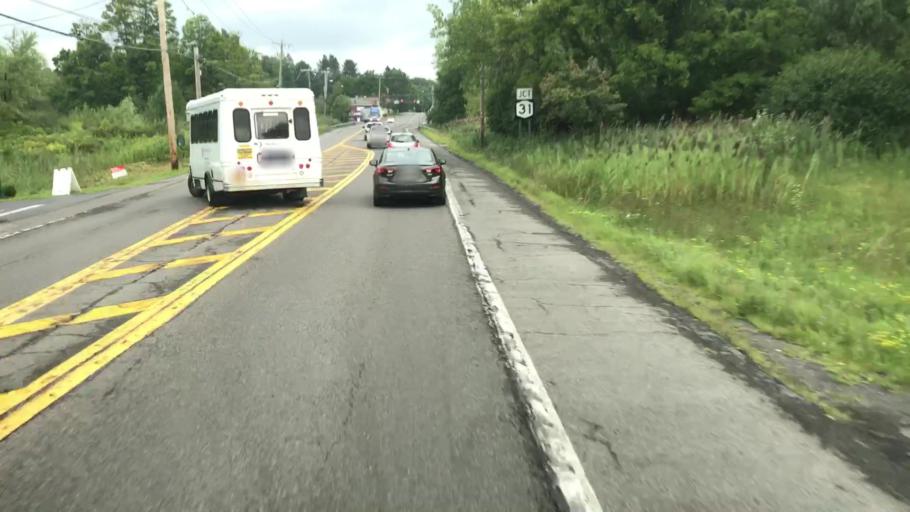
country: US
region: New York
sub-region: Onondaga County
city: Liverpool
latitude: 43.1839
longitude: -76.2167
